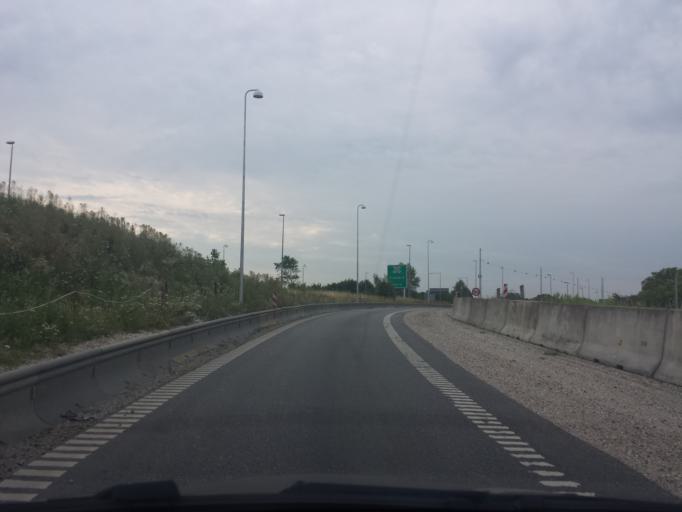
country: DK
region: Capital Region
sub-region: Brondby Kommune
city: Brondbyvester
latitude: 55.6400
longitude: 12.4246
